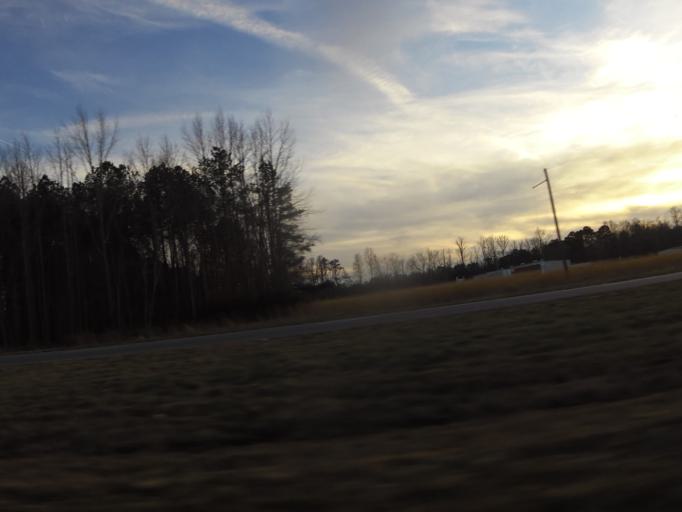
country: US
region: Virginia
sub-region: Southampton County
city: Courtland
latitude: 36.6825
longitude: -77.0107
